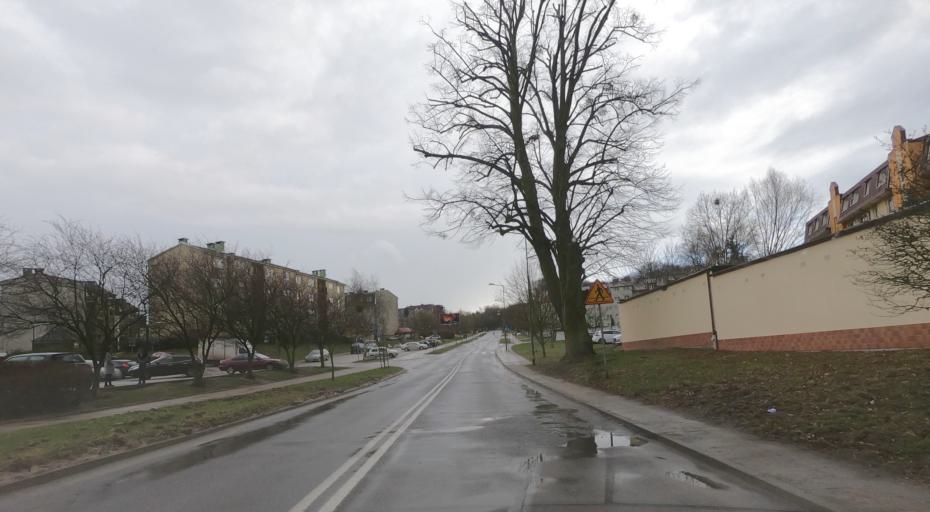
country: PL
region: West Pomeranian Voivodeship
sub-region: Szczecin
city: Szczecin
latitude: 53.3678
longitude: 14.6465
